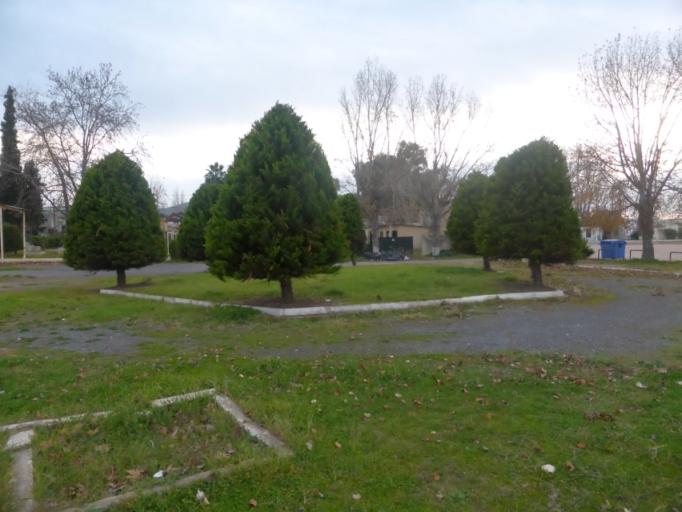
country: GR
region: Attica
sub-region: Nomarchia Anatolikis Attikis
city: Skala Oropou
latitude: 38.3229
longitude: 23.7838
